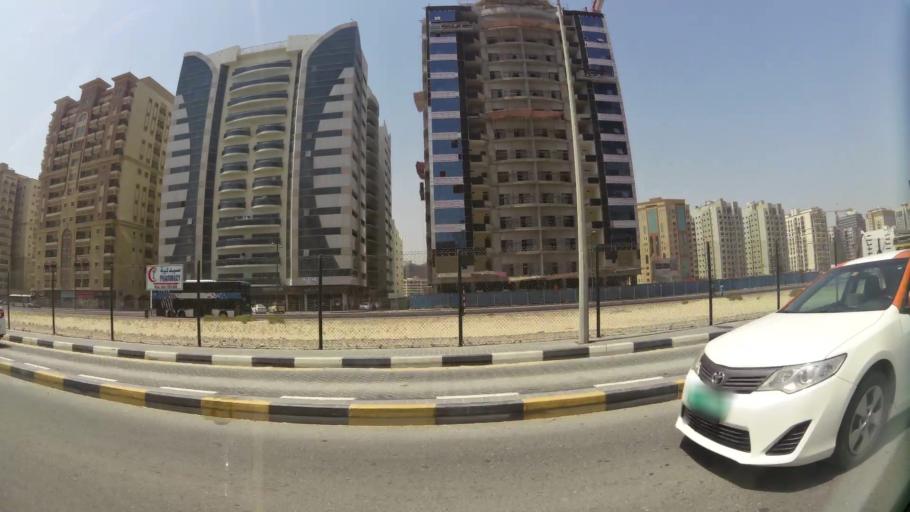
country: AE
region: Ash Shariqah
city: Sharjah
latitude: 25.2975
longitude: 55.3683
